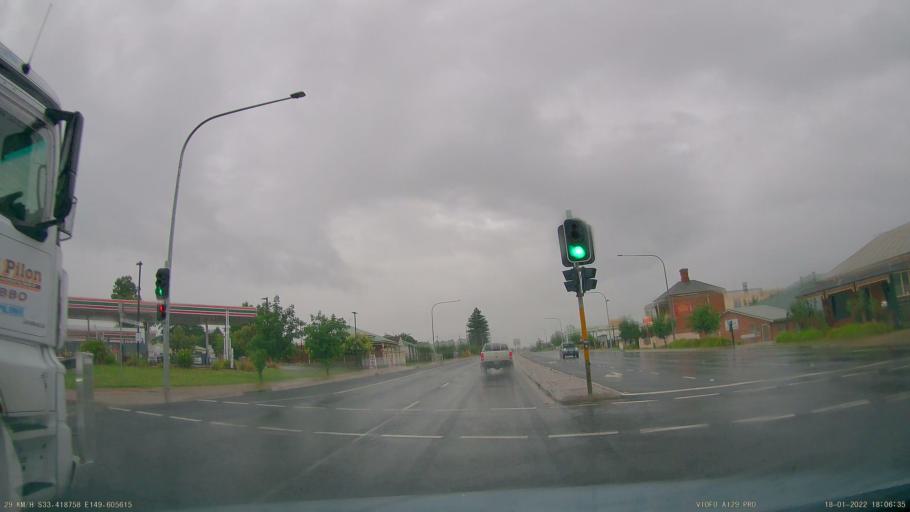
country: AU
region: New South Wales
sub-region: Bathurst Regional
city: Kelso
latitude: -33.4188
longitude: 149.6057
